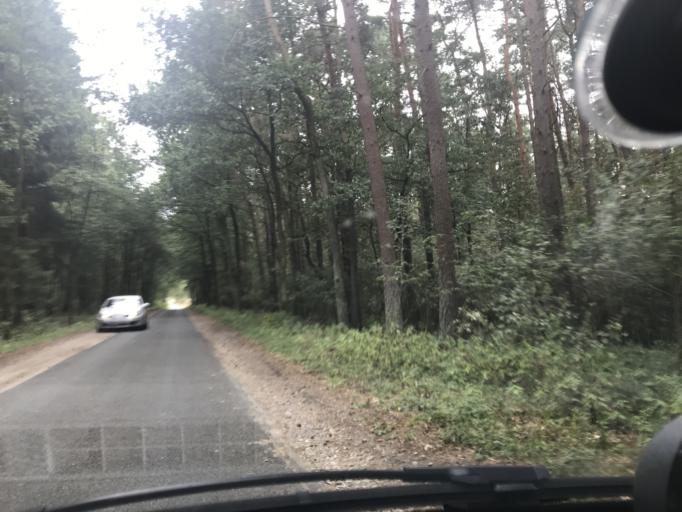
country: DE
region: Lower Saxony
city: Moisburg
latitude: 53.3923
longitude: 9.7249
